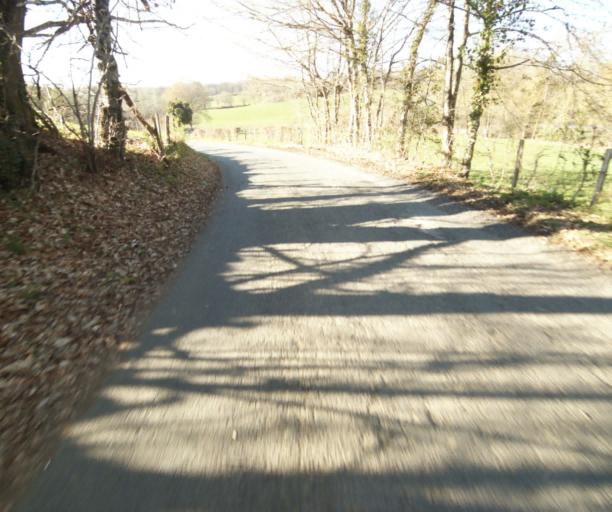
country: FR
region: Limousin
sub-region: Departement de la Correze
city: Seilhac
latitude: 45.3806
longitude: 1.7108
